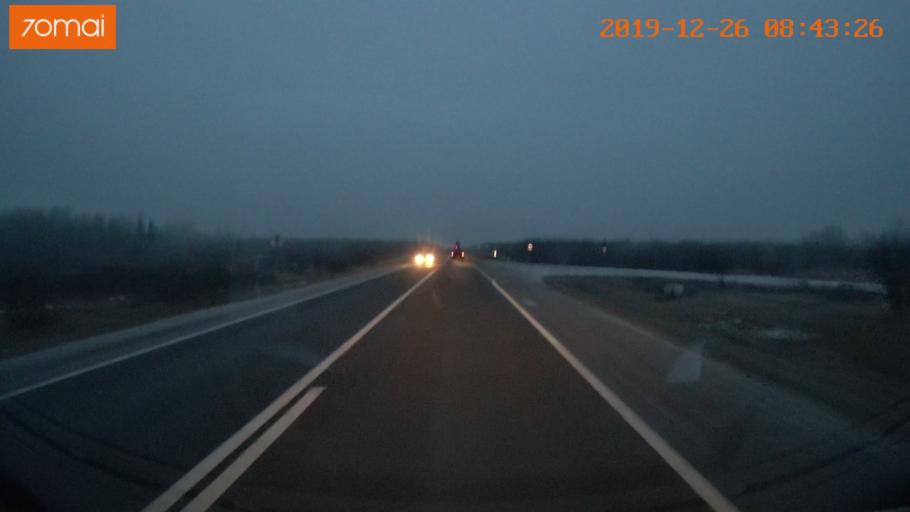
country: RU
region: Jaroslavl
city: Prechistoye
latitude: 58.5729
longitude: 40.3532
